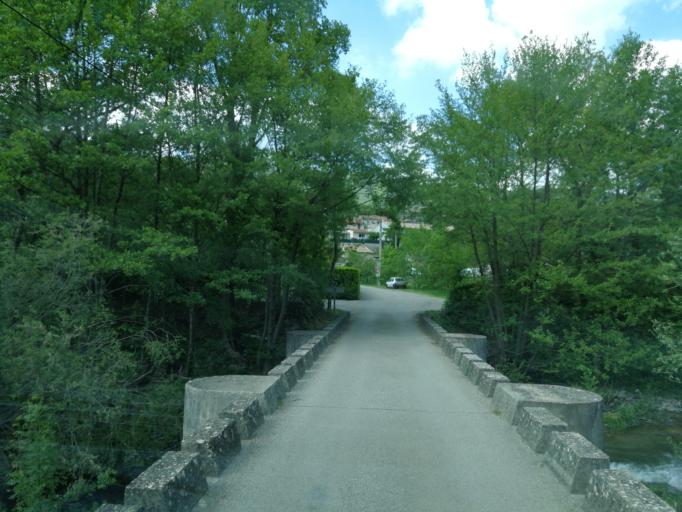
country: FR
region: Rhone-Alpes
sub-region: Departement de l'Ardeche
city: Flaviac
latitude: 44.7439
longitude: 4.6705
